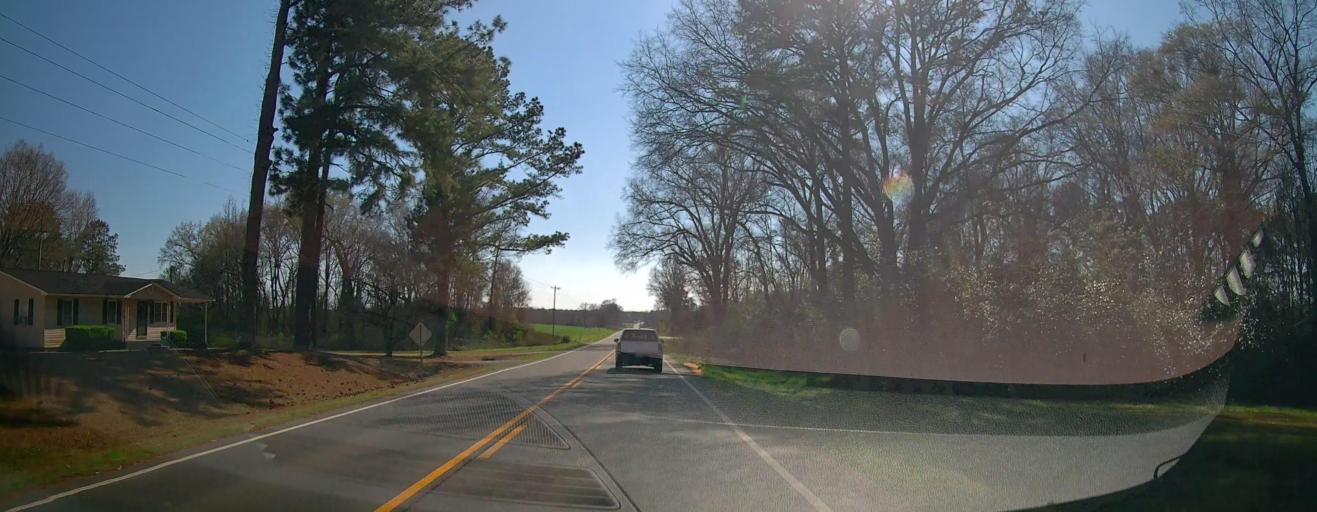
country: US
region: Georgia
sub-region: Macon County
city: Montezuma
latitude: 32.3073
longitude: -83.9057
